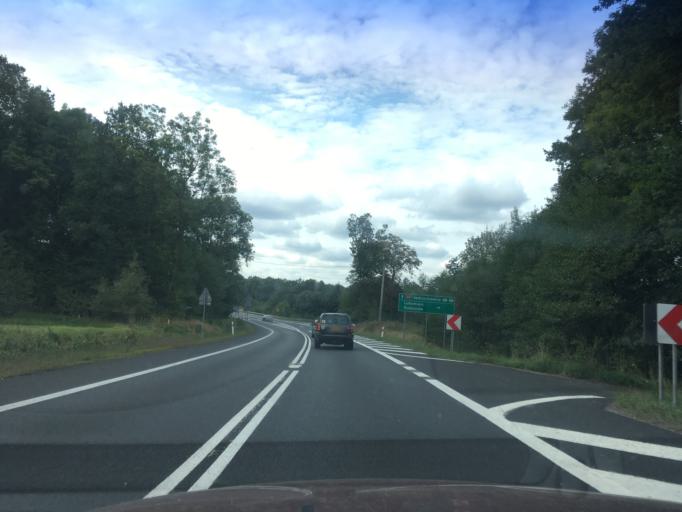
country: PL
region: Lower Silesian Voivodeship
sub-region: Powiat lwowecki
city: Lubomierz
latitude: 50.9976
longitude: 15.4754
